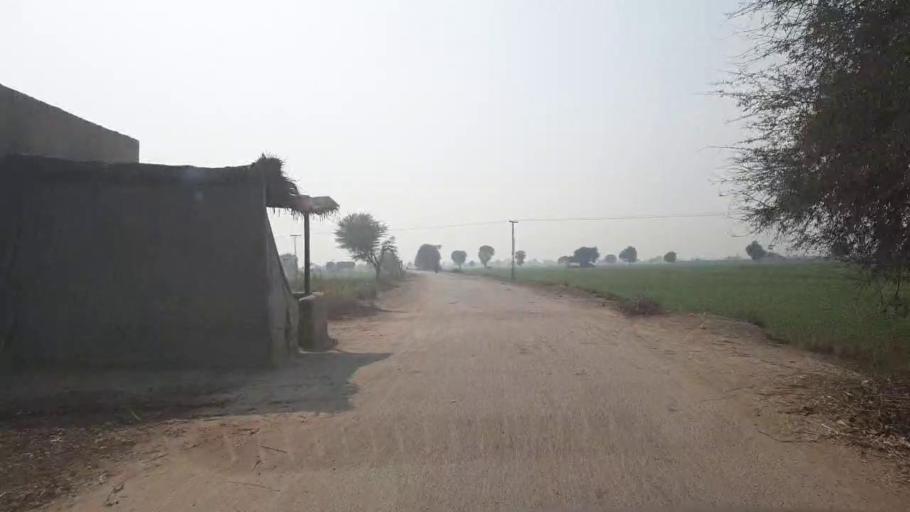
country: PK
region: Sindh
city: Hala
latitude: 25.8773
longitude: 68.4339
